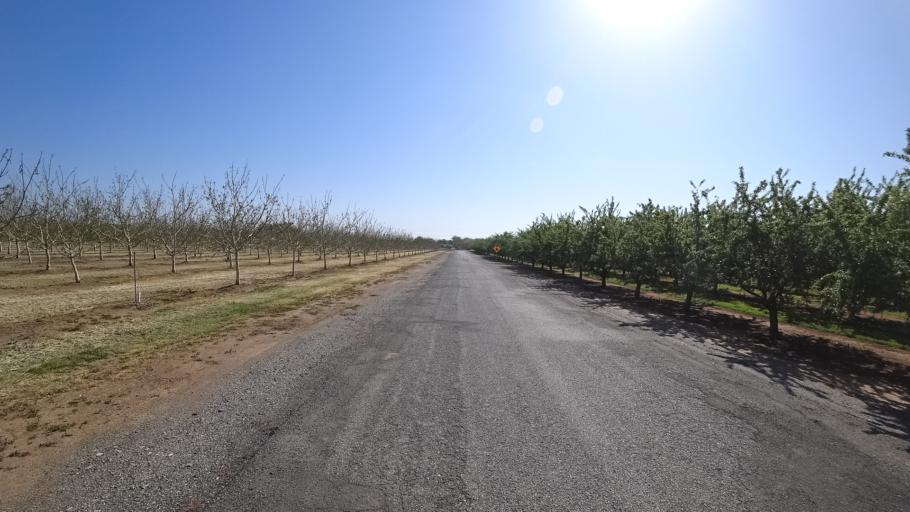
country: US
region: California
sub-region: Glenn County
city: Hamilton City
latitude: 39.6451
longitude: -122.0102
